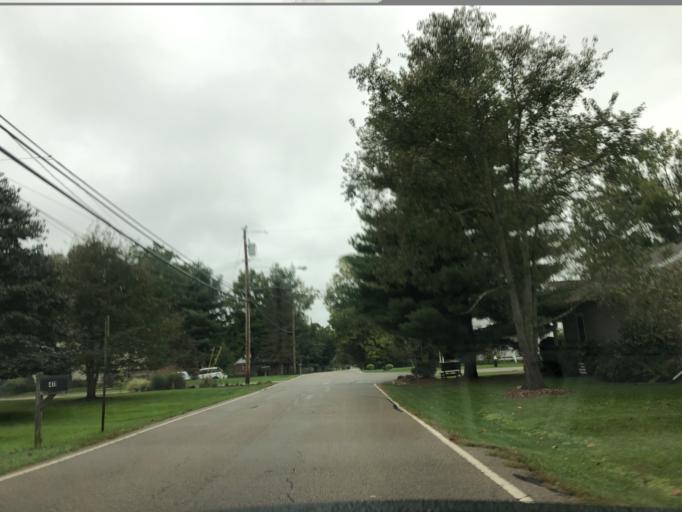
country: US
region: Ohio
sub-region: Hamilton County
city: Loveland
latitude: 39.2614
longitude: -84.2540
